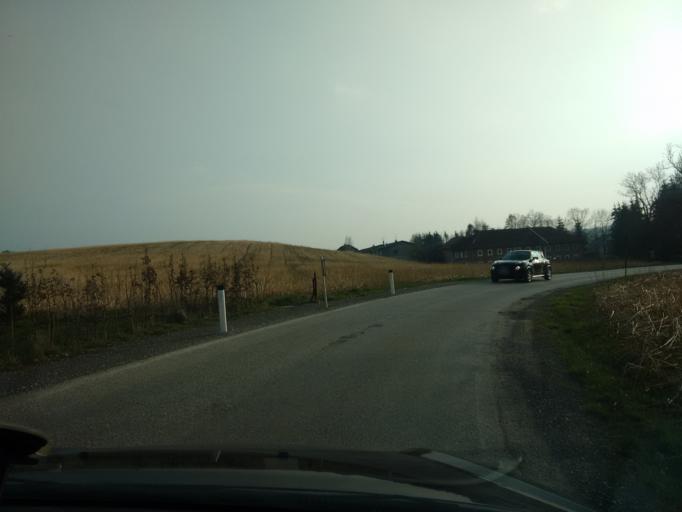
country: AT
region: Upper Austria
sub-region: Politischer Bezirk Grieskirchen
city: Bad Schallerbach
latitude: 48.2145
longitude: 13.9571
